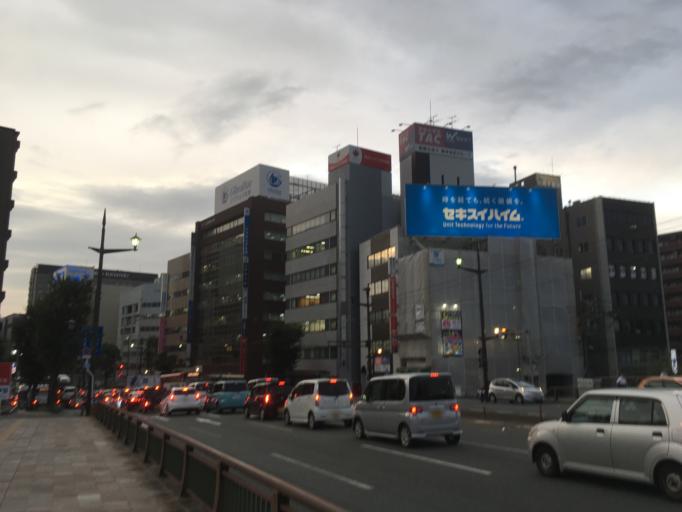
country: JP
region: Kumamoto
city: Kumamoto
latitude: 32.8016
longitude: 130.7146
